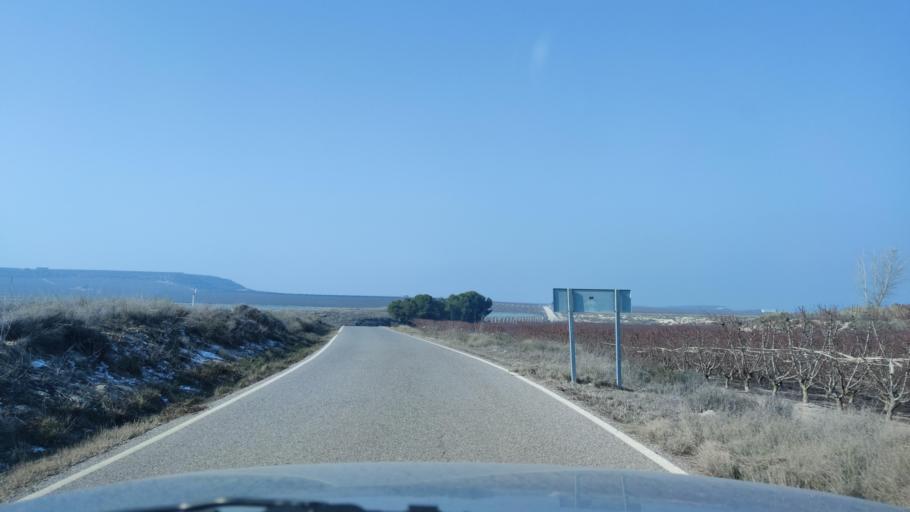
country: ES
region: Catalonia
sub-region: Provincia de Lleida
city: Sunyer
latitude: 41.5298
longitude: 0.5796
